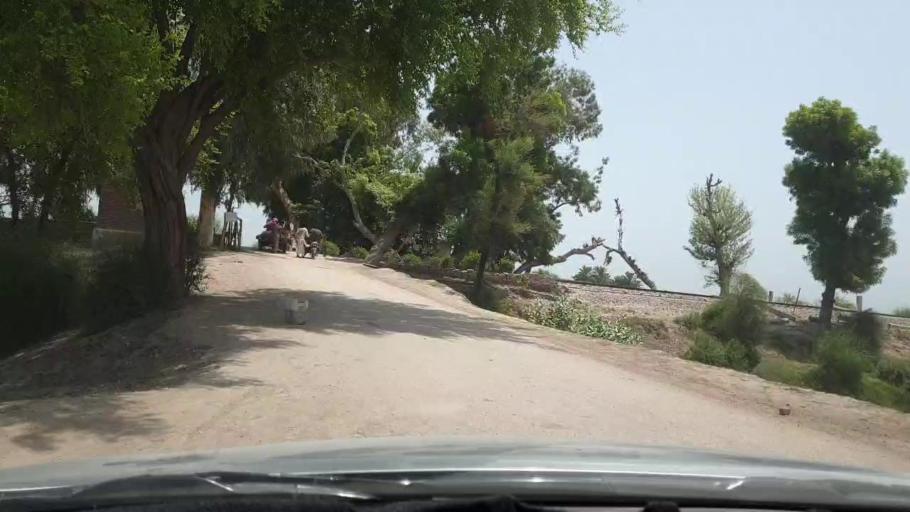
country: PK
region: Sindh
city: Pano Aqil
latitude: 27.8850
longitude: 69.1431
